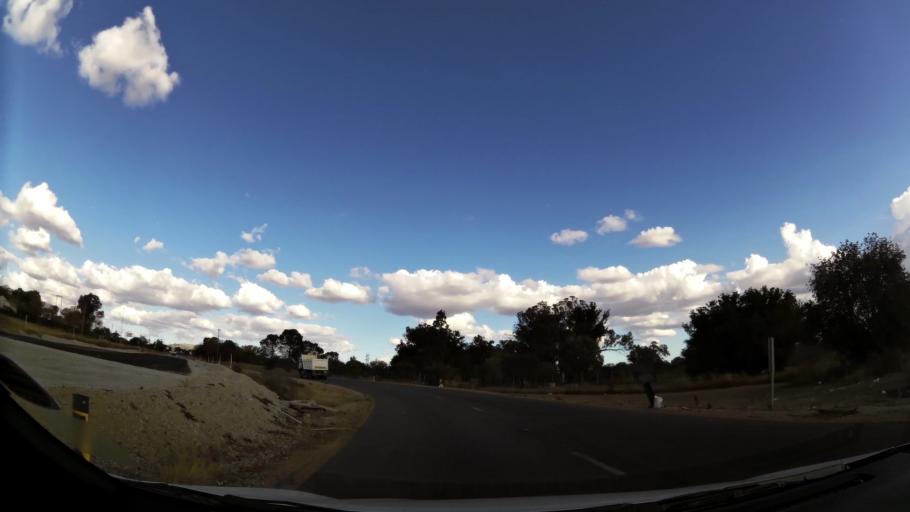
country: ZA
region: Limpopo
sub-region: Capricorn District Municipality
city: Polokwane
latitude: -23.9339
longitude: 29.4719
